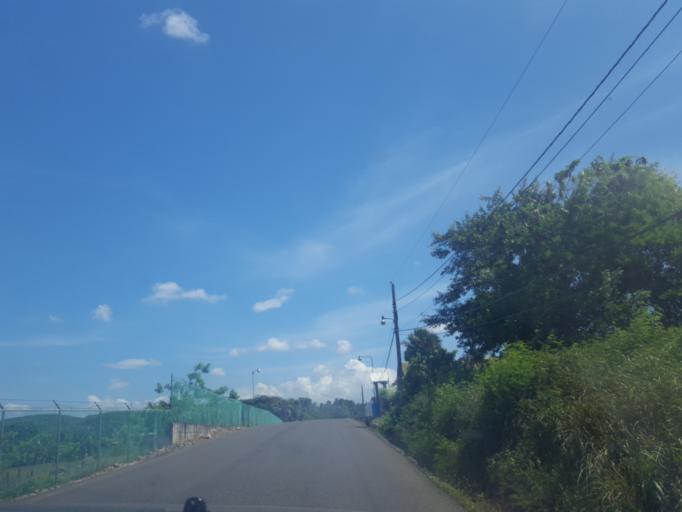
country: DO
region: Santiago
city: Licey al Medio
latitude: 19.3885
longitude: -70.6495
